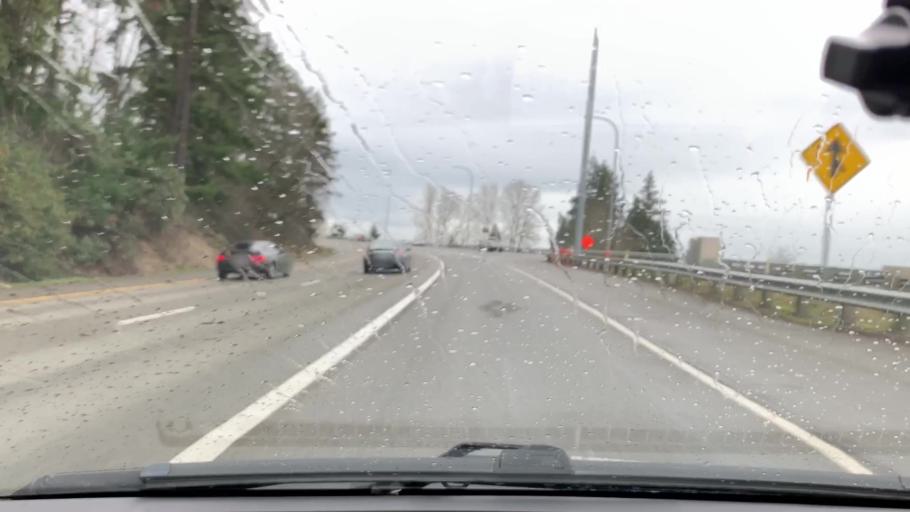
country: US
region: Washington
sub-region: King County
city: Bellevue
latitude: 47.6308
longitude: -122.1721
